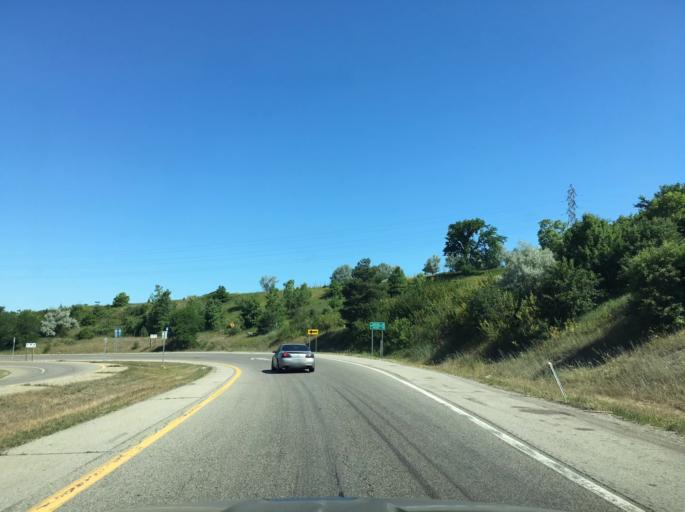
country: US
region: Michigan
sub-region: Oakland County
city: Auburn Hills
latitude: 42.7021
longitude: -83.2822
